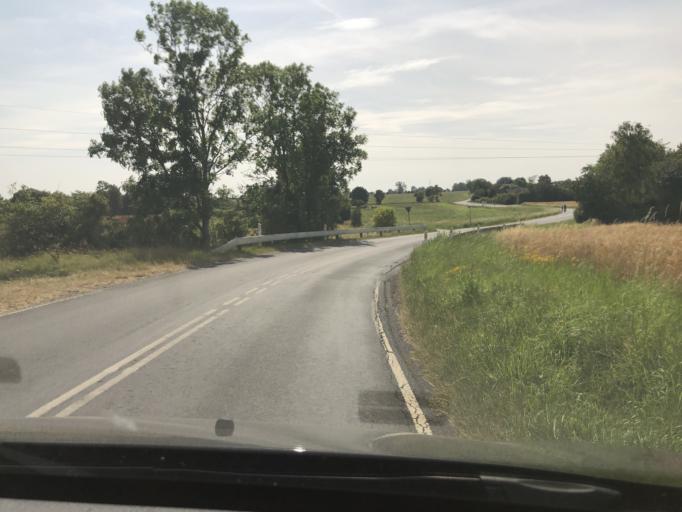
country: DK
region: South Denmark
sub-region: AEro Kommune
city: AEroskobing
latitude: 54.8724
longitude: 10.3956
